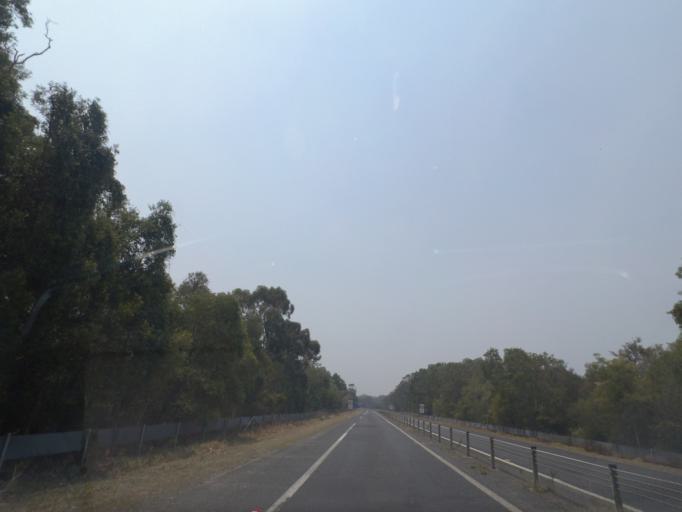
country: AU
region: New South Wales
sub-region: Ballina
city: Ballina
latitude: -28.9323
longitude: 153.4735
